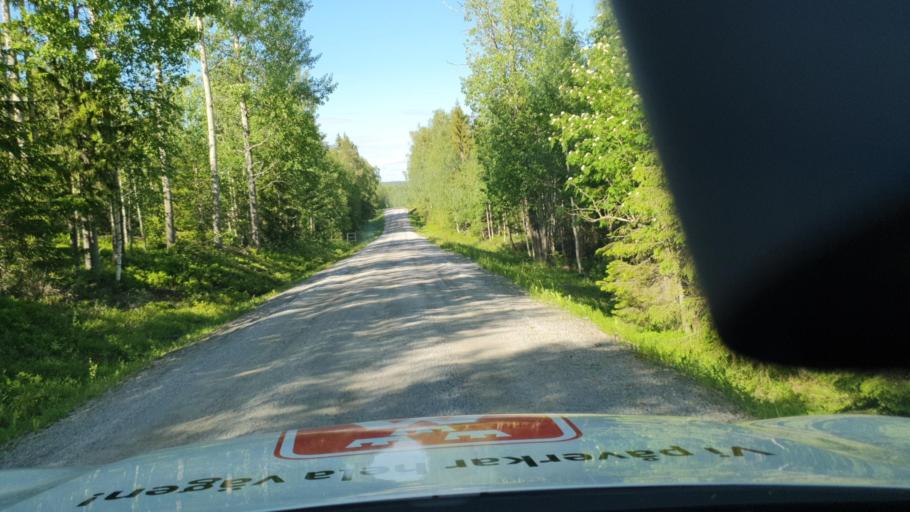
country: SE
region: Vaesterbotten
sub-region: Vannas Kommun
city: Vaennaes
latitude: 63.8001
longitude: 19.6333
